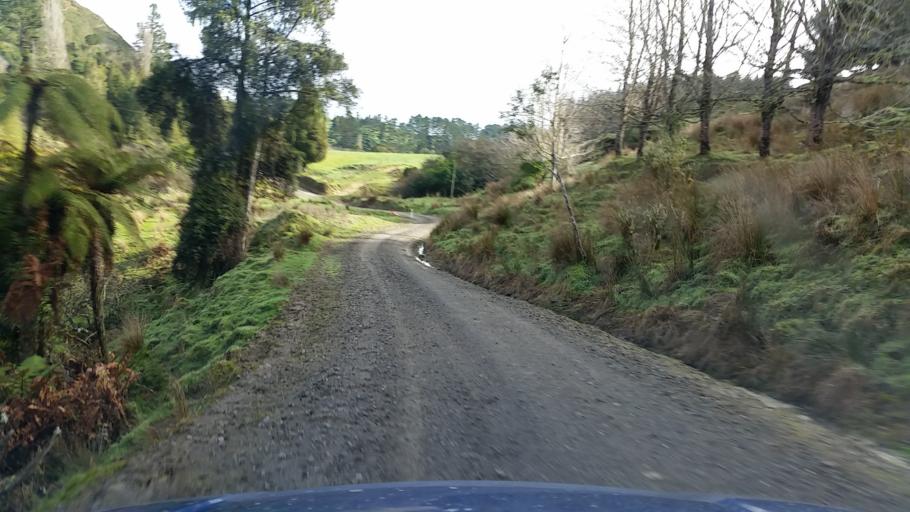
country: NZ
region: Taranaki
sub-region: New Plymouth District
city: Waitara
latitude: -39.1119
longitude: 174.8525
